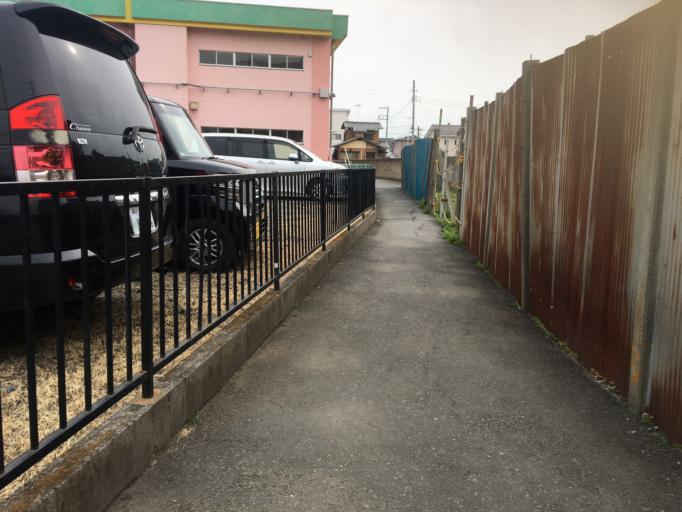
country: JP
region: Saitama
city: Kazo
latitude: 36.1234
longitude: 139.6038
